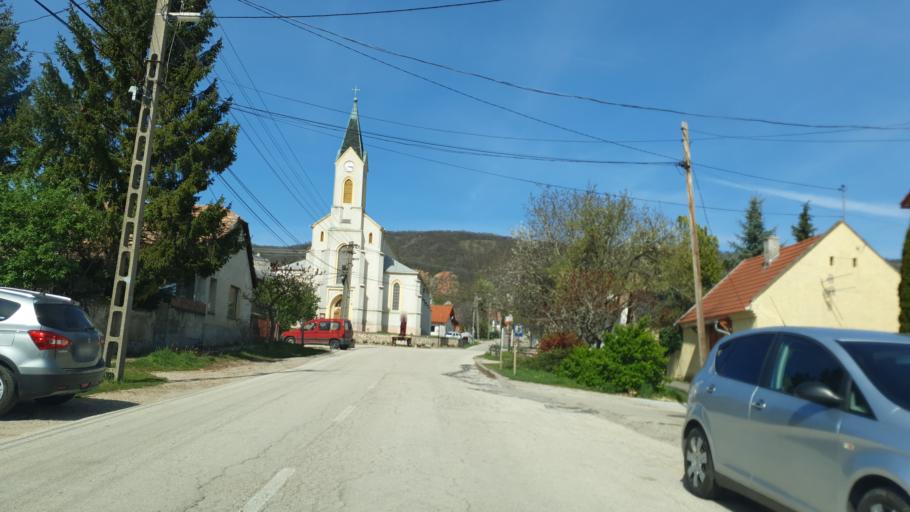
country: HU
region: Fejer
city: Bodajk
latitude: 47.3528
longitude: 18.2723
